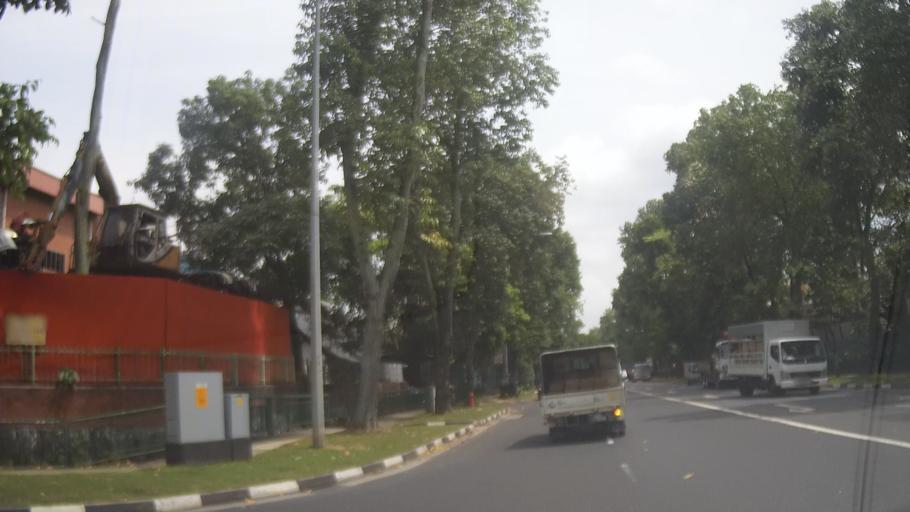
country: MY
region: Johor
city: Johor Bahru
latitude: 1.4158
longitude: 103.7442
